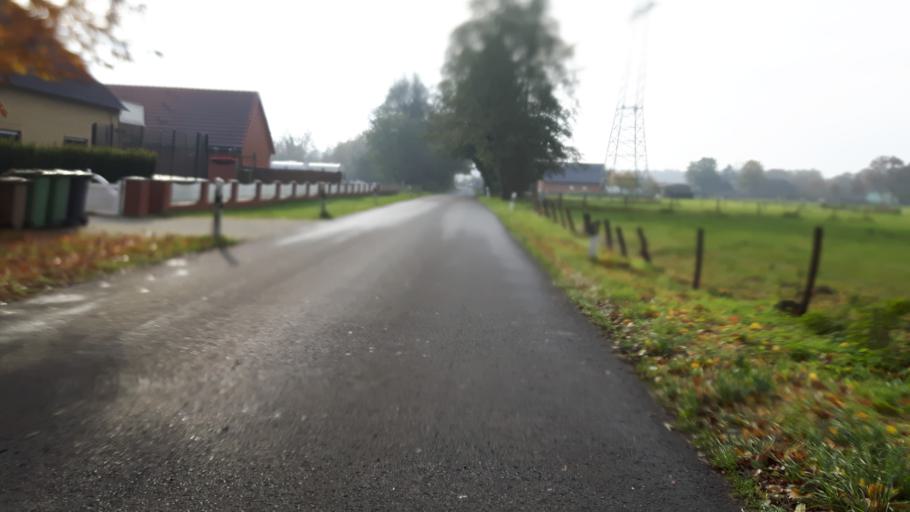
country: DE
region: Lower Saxony
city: Delmenhorst
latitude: 53.0180
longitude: 8.5867
